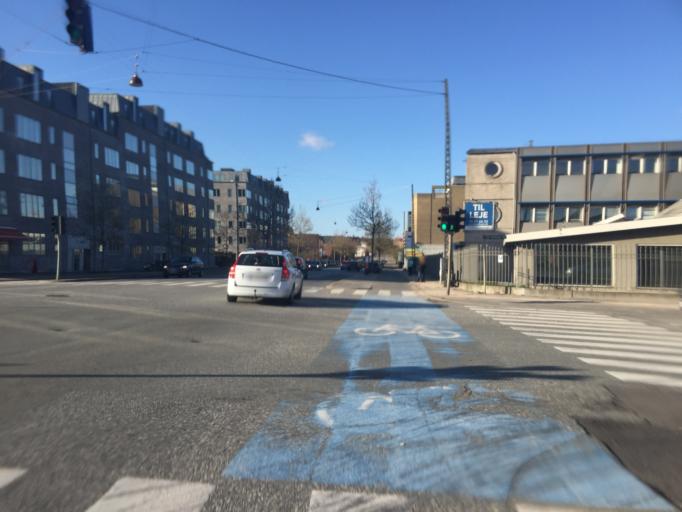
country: DK
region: Capital Region
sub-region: Frederiksberg Kommune
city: Frederiksberg
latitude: 55.6557
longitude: 12.5122
